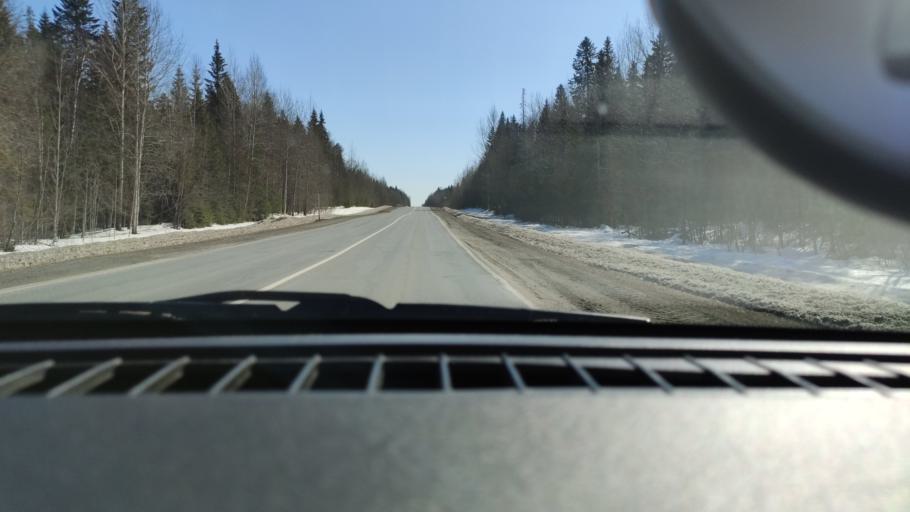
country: RU
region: Perm
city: Perm
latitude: 58.1618
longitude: 56.2445
